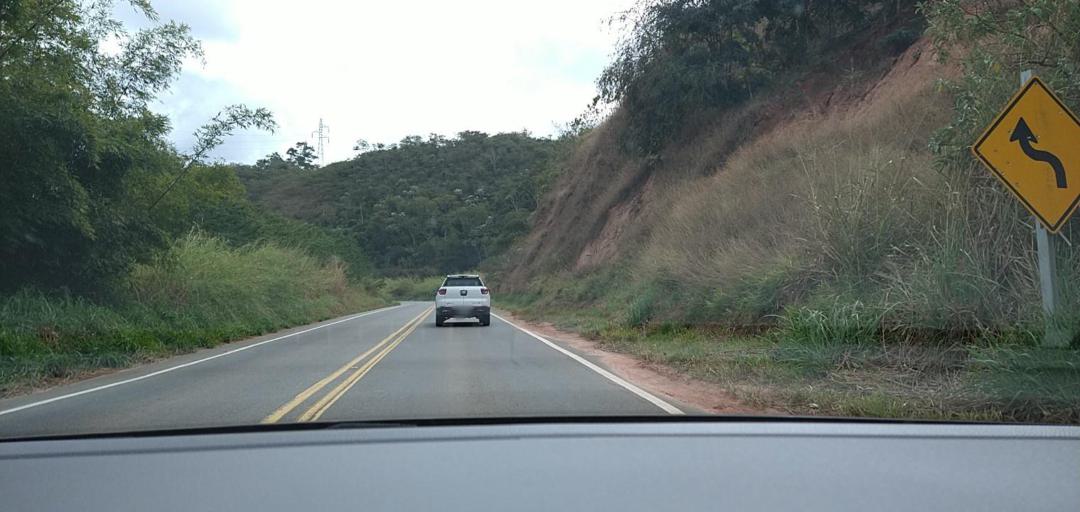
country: BR
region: Minas Gerais
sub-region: Ponte Nova
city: Ponte Nova
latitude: -20.5325
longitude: -42.8927
